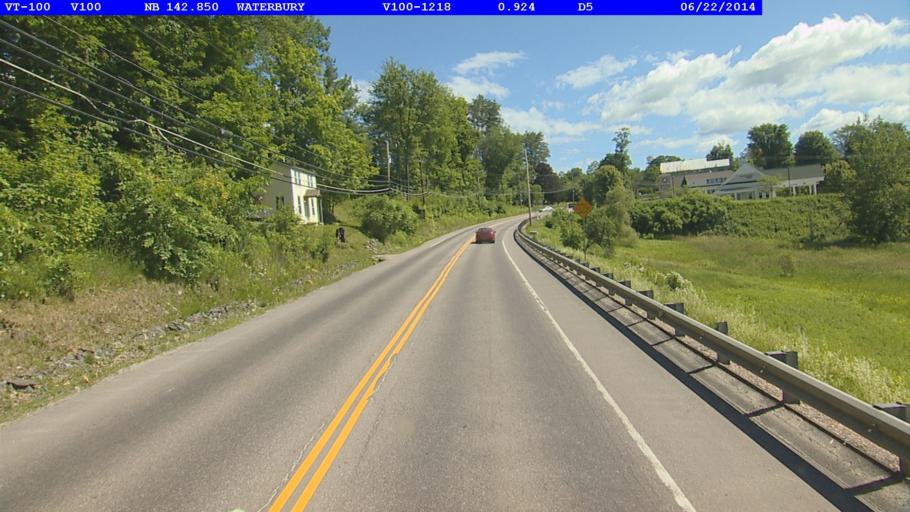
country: US
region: Vermont
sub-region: Washington County
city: Waterbury
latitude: 44.3481
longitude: -72.7450
